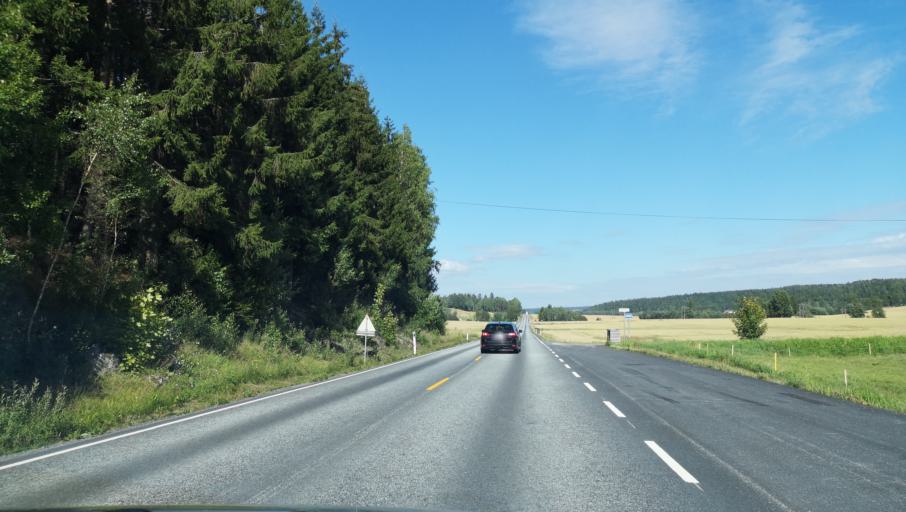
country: NO
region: Ostfold
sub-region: Hobol
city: Elvestad
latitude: 59.5916
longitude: 10.8879
